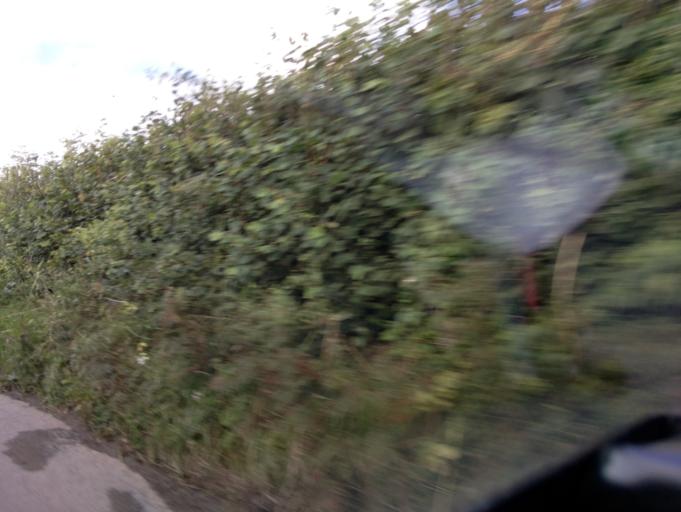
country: GB
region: England
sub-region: Devon
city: South Brent
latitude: 50.3869
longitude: -3.7689
